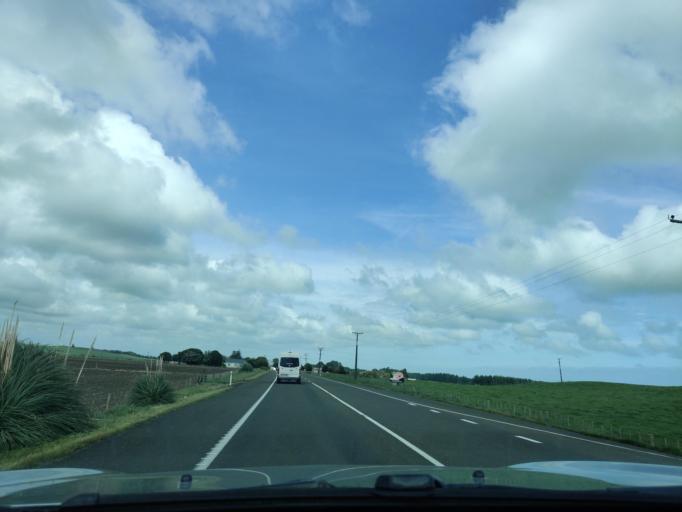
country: NZ
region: Manawatu-Wanganui
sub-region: Wanganui District
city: Wanganui
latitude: -39.8157
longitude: 174.8273
